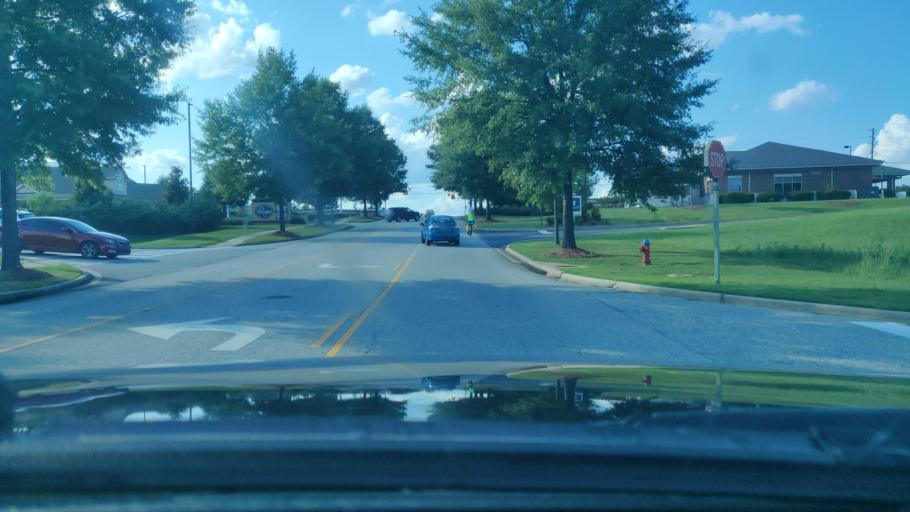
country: US
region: Alabama
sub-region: Lee County
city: Opelika
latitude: 32.6207
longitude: -85.4092
